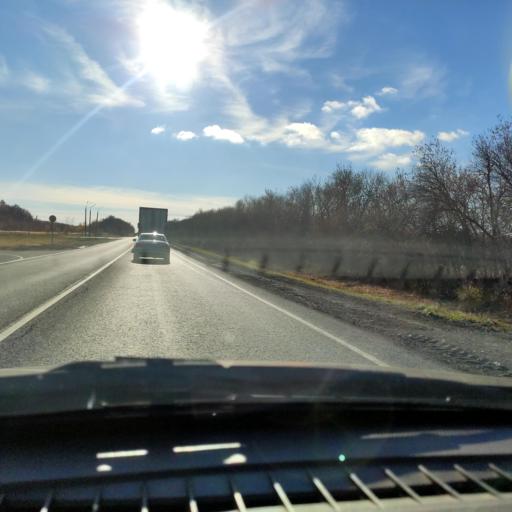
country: RU
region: Samara
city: Zhigulevsk
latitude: 53.3164
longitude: 49.3638
